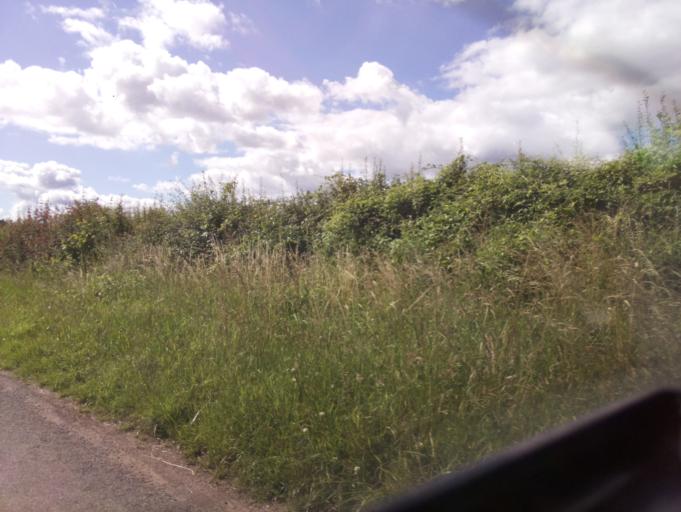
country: GB
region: England
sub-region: Gloucestershire
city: Mitcheldean
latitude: 51.8409
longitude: -2.4318
